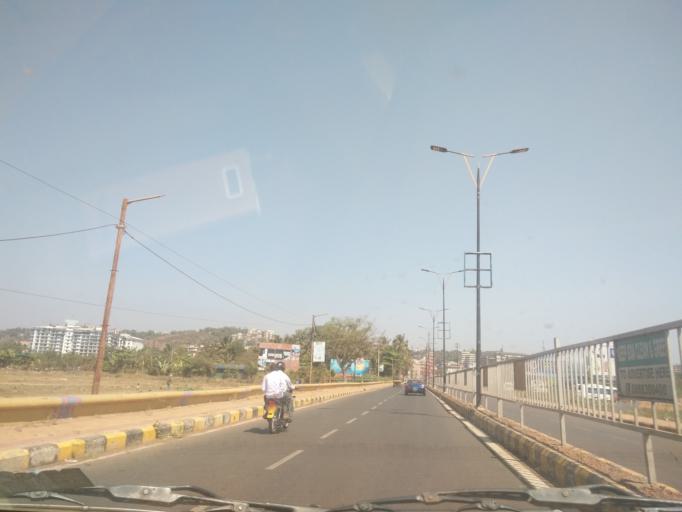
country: IN
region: Goa
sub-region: North Goa
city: Mapuca
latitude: 15.5855
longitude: 73.8078
